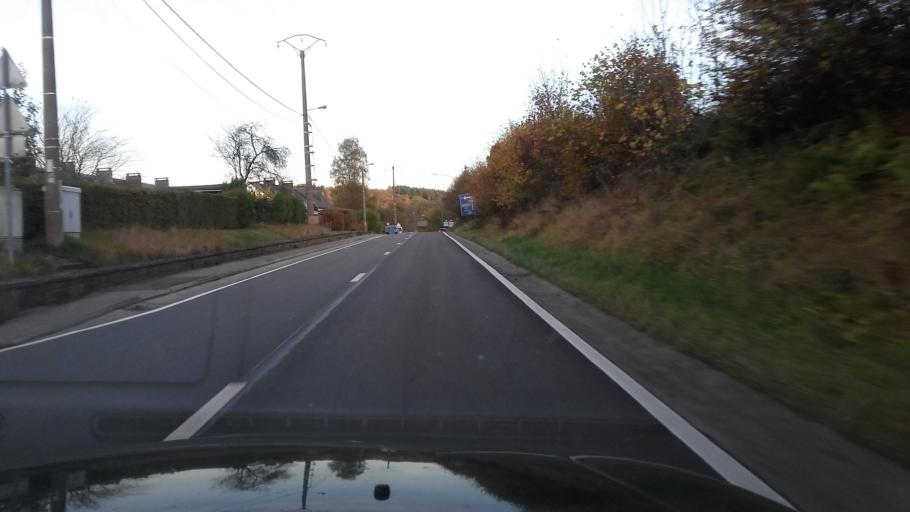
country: BE
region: Wallonia
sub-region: Province du Luxembourg
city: Bouillon
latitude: 49.7841
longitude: 5.0730
